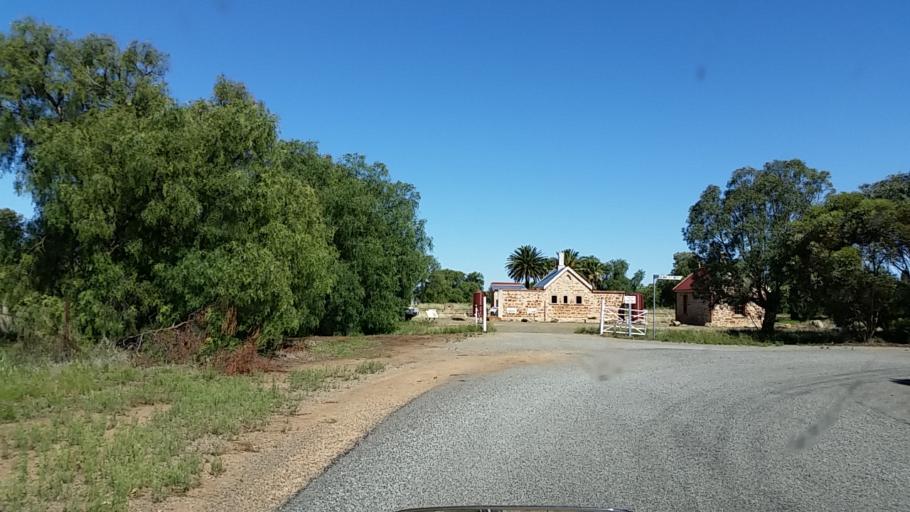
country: AU
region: South Australia
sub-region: Peterborough
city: Peterborough
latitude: -33.1499
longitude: 138.9208
